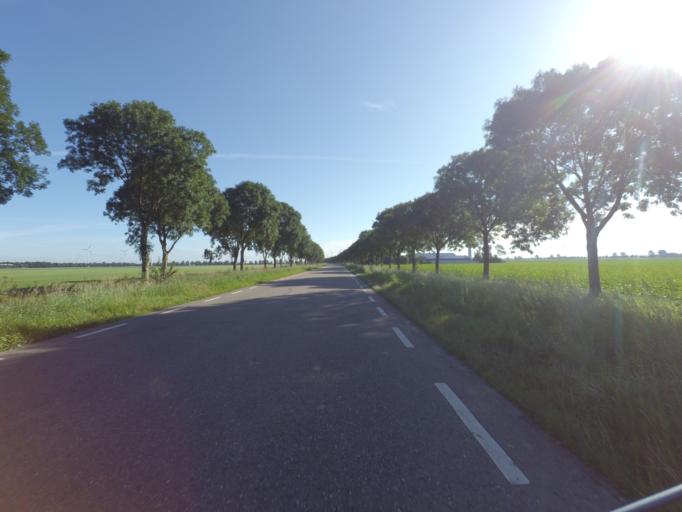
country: NL
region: Flevoland
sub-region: Gemeente Zeewolde
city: Zeewolde
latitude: 52.3688
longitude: 5.4954
